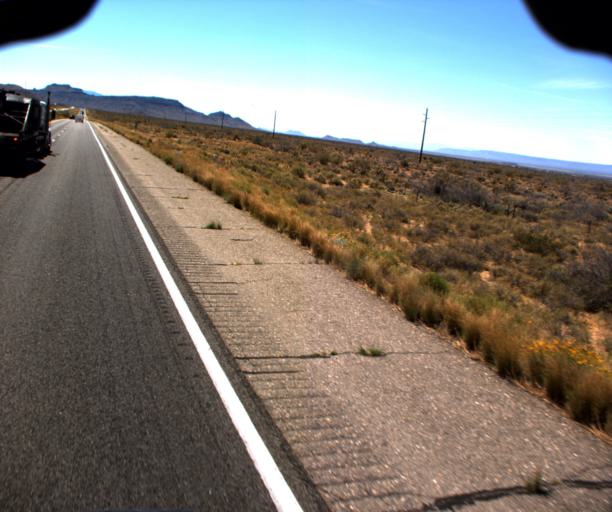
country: US
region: Arizona
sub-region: Mohave County
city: Golden Valley
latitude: 35.2696
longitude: -114.1674
